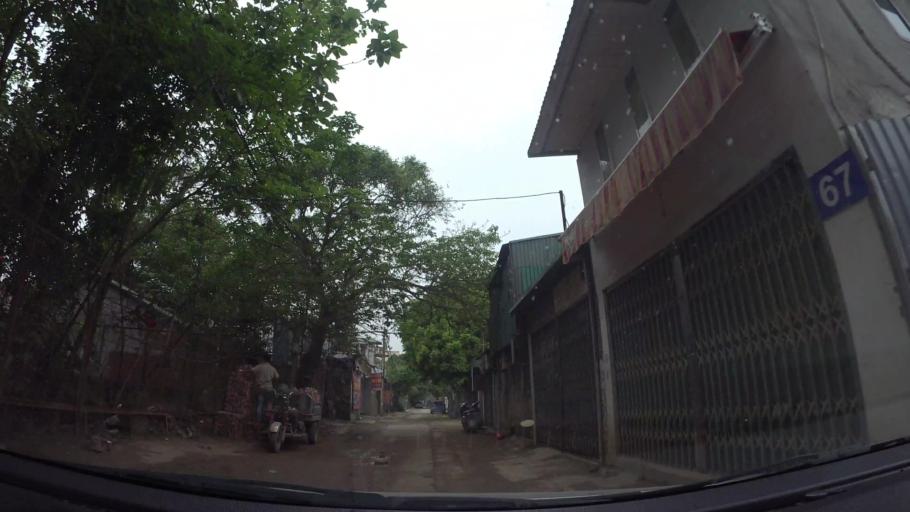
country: VN
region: Ha Noi
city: Tay Ho
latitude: 21.0637
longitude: 105.8380
